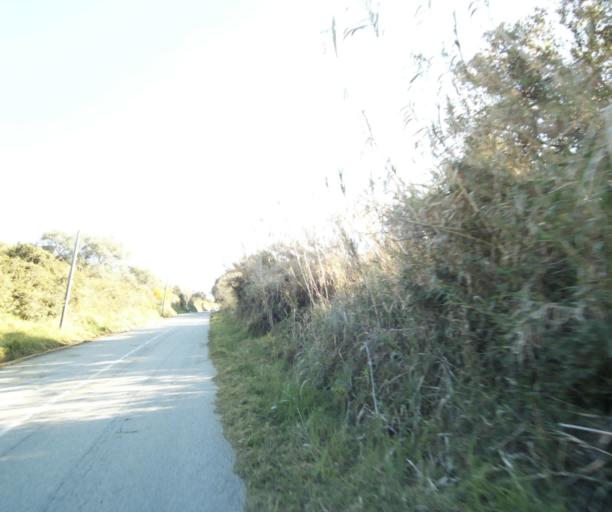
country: FR
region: Corsica
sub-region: Departement de la Corse-du-Sud
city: Propriano
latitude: 41.6672
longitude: 8.8952
